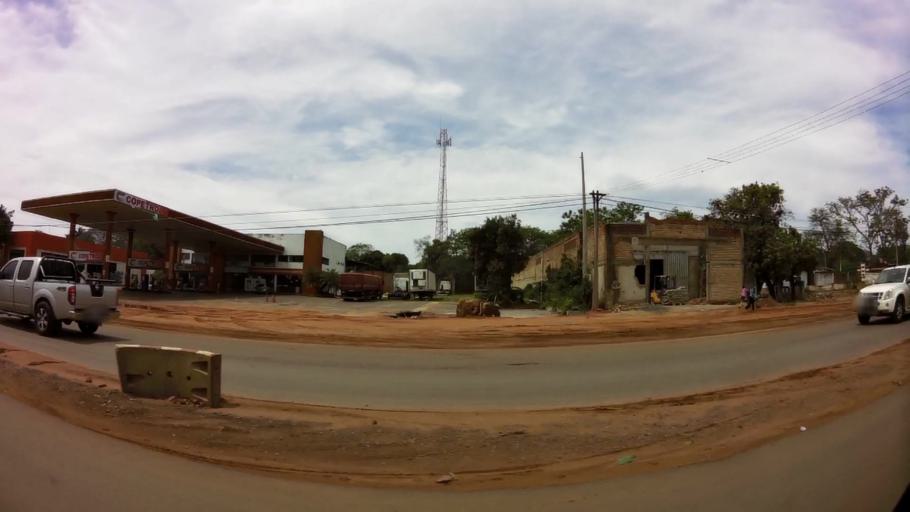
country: PY
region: Central
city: Limpio
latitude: -25.1974
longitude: -57.5154
